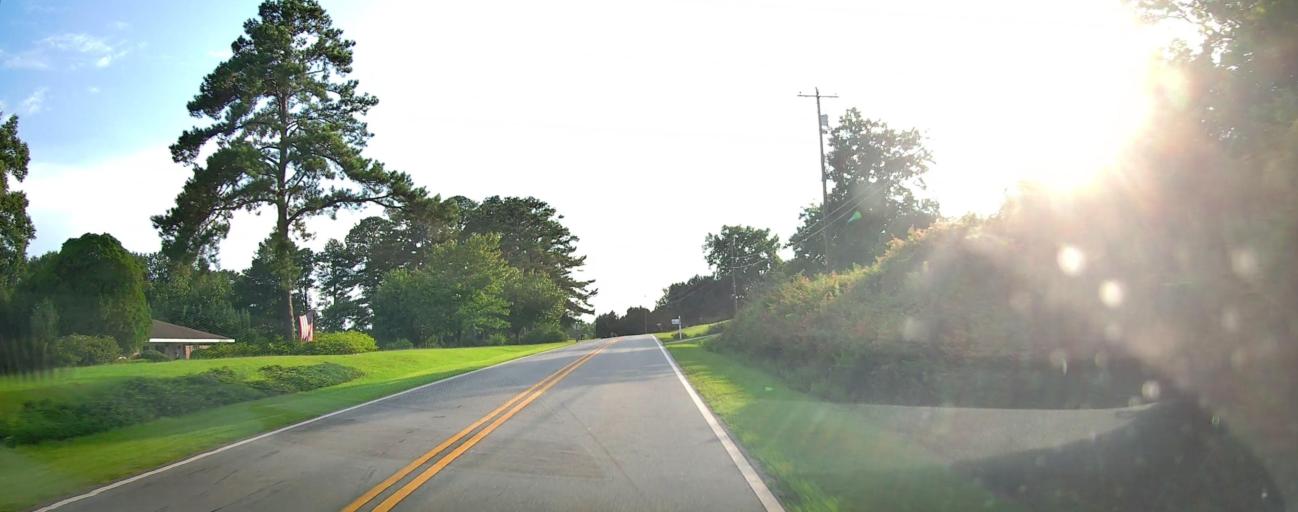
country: US
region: Georgia
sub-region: Peach County
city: Byron
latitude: 32.7349
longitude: -83.7369
